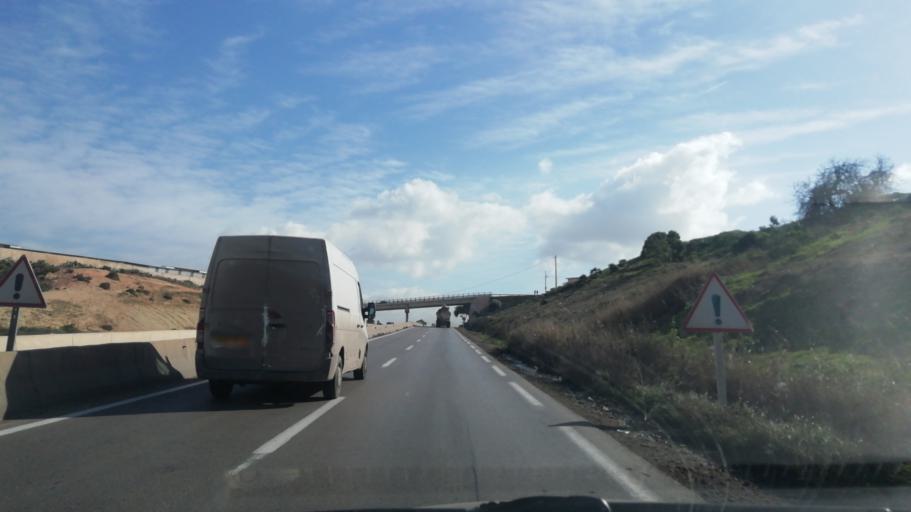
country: DZ
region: Oran
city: Ain el Bya
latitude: 35.7673
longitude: -0.2235
